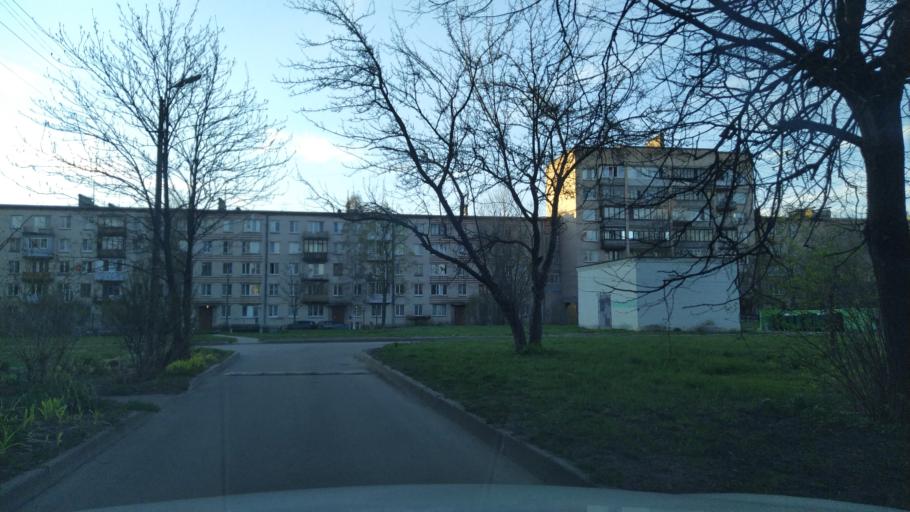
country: RU
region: St.-Petersburg
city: Pushkin
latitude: 59.7048
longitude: 30.3662
